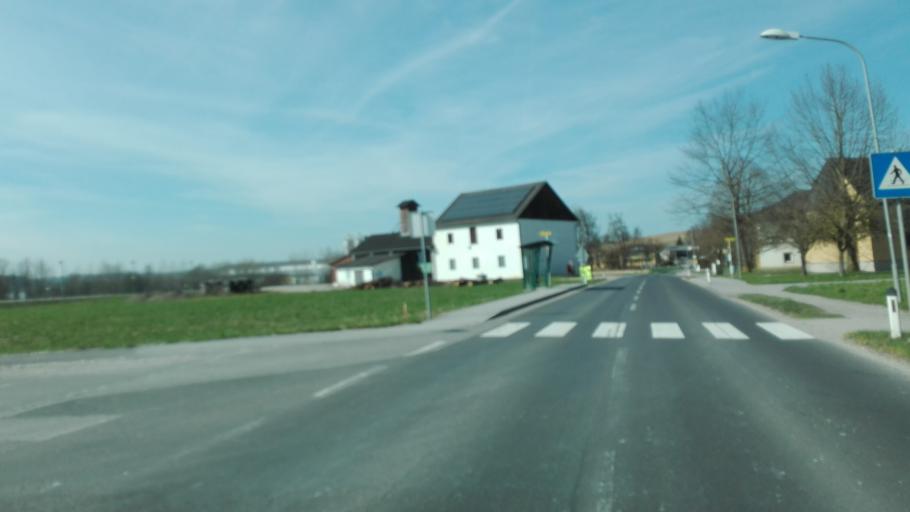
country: AT
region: Upper Austria
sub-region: Politischer Bezirk Perg
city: Perg
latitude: 48.2571
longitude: 14.5915
